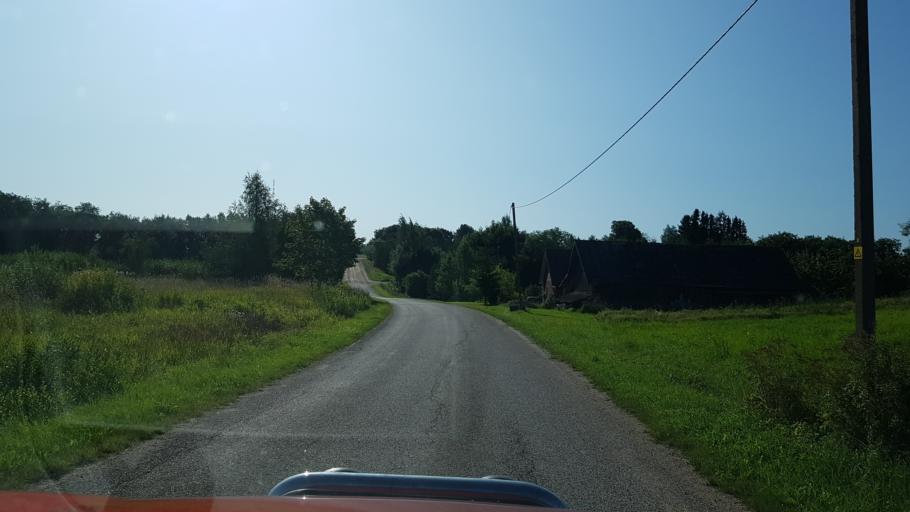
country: LV
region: Apes Novads
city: Ape
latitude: 57.6075
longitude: 26.8410
